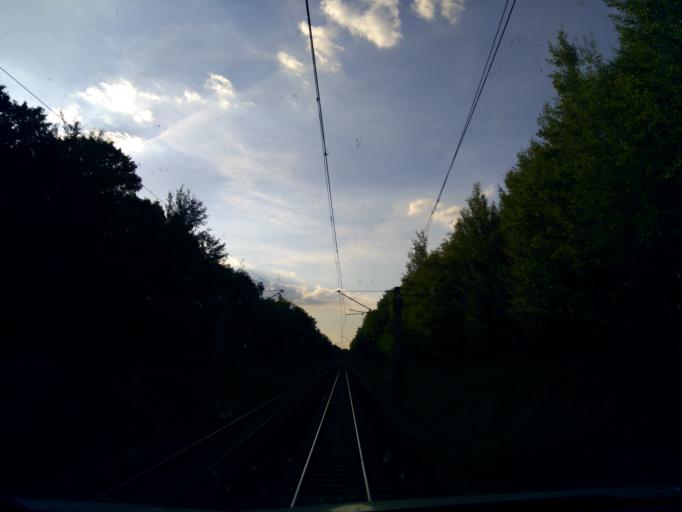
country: DE
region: Mecklenburg-Vorpommern
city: Ludwigslust
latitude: 53.3059
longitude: 11.5255
